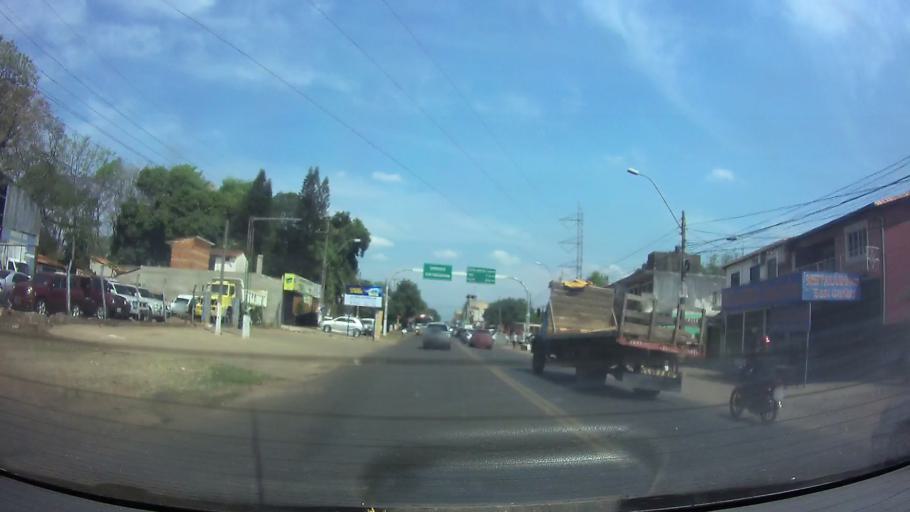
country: PY
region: Central
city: San Lorenzo
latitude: -25.3613
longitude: -57.4844
